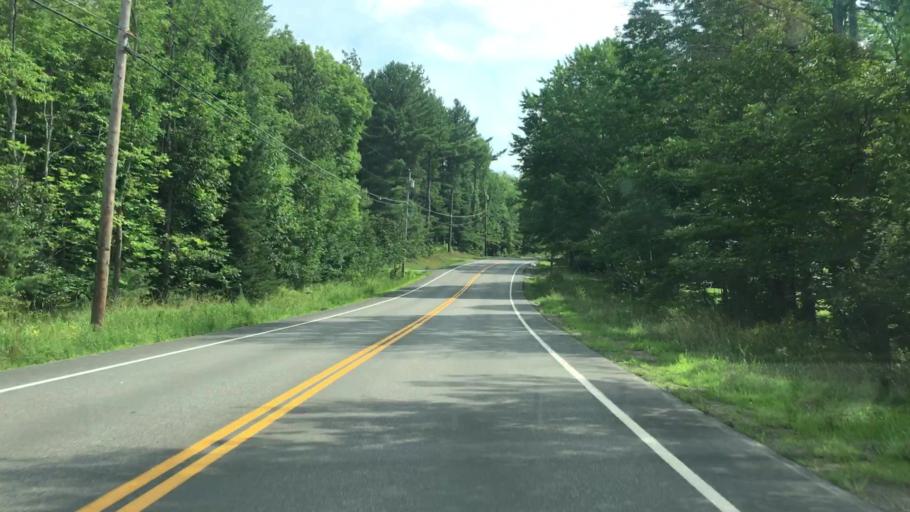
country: US
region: Maine
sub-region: Kennebec County
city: Windsor
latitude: 44.3317
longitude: -69.5809
